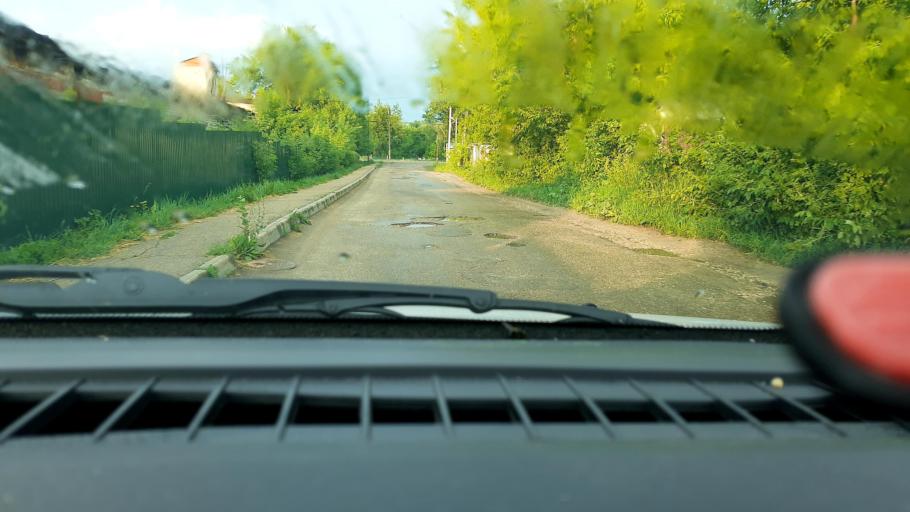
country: RU
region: Nizjnij Novgorod
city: Lukoyanov
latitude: 55.0416
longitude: 44.4954
